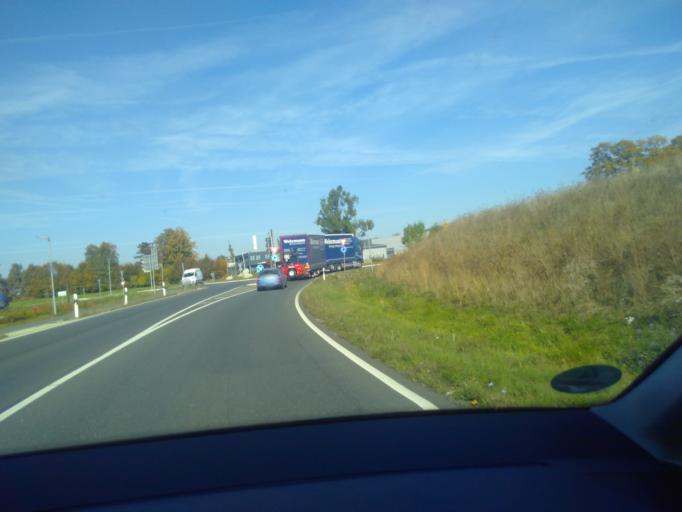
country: DE
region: North Rhine-Westphalia
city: Halle
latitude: 52.0334
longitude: 8.3744
